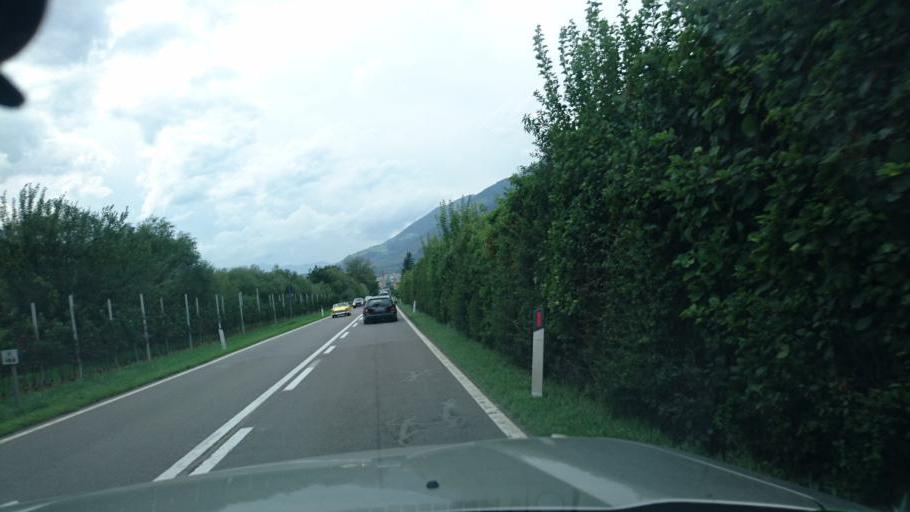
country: IT
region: Trentino-Alto Adige
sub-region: Bolzano
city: Silandro
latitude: 46.6252
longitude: 10.7969
